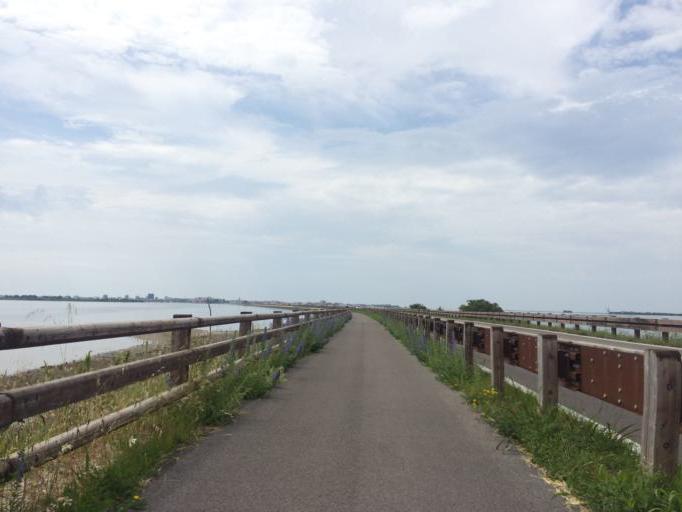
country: IT
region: Friuli Venezia Giulia
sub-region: Provincia di Gorizia
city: Grado
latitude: 45.7086
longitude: 13.3830
